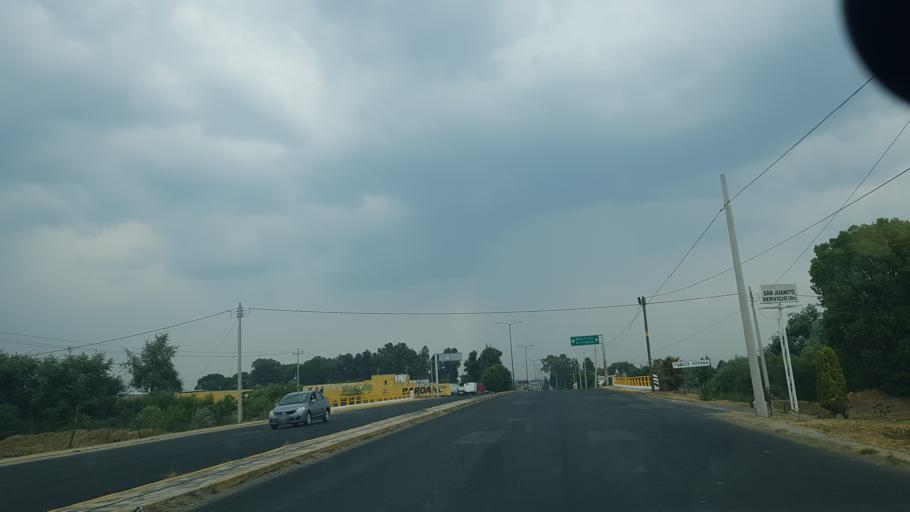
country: MX
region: Puebla
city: Huejotzingo
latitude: 19.1723
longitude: -98.4131
